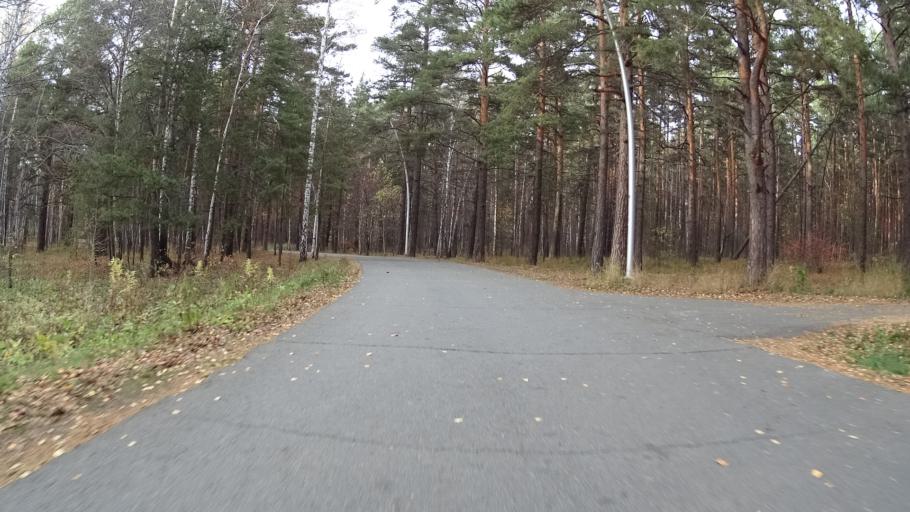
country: RU
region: Chelyabinsk
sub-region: Gorod Chelyabinsk
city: Chelyabinsk
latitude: 55.1391
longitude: 61.3514
